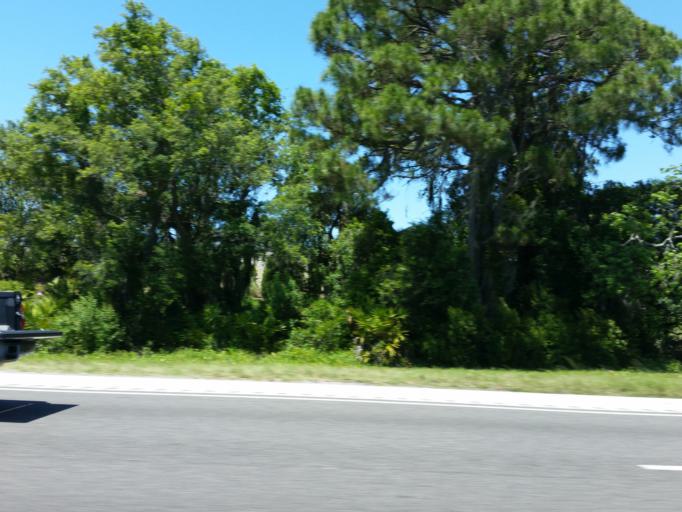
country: US
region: Florida
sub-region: Sarasota County
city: Lake Sarasota
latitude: 27.2496
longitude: -82.4498
